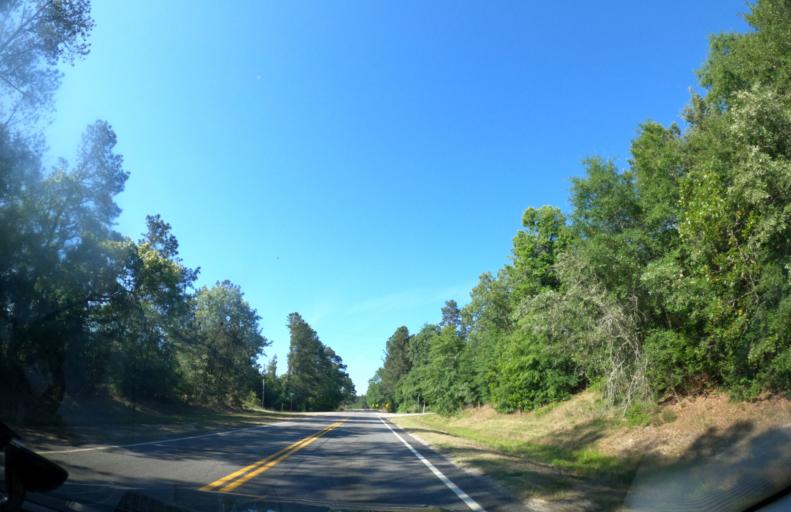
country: US
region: Georgia
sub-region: Columbia County
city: Harlem
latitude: 33.3723
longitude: -82.3226
